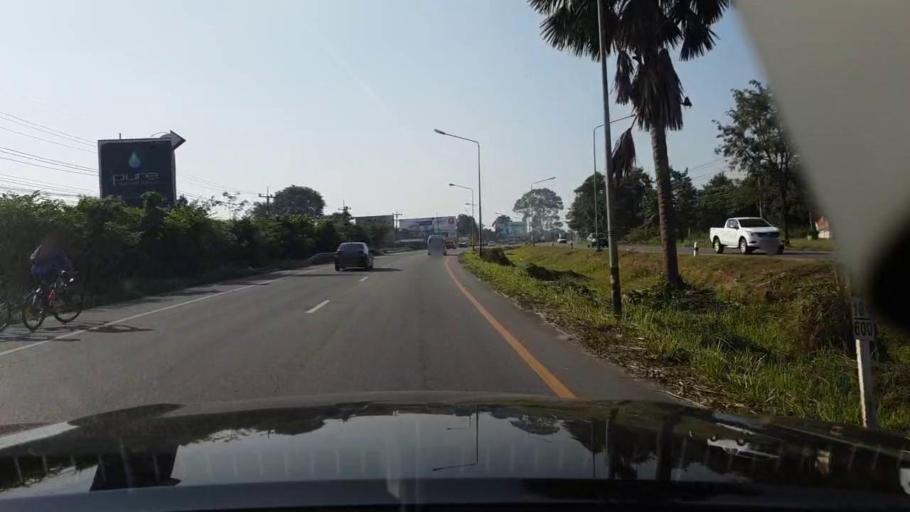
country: TH
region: Chon Buri
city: Sattahip
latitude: 12.7919
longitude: 100.9179
